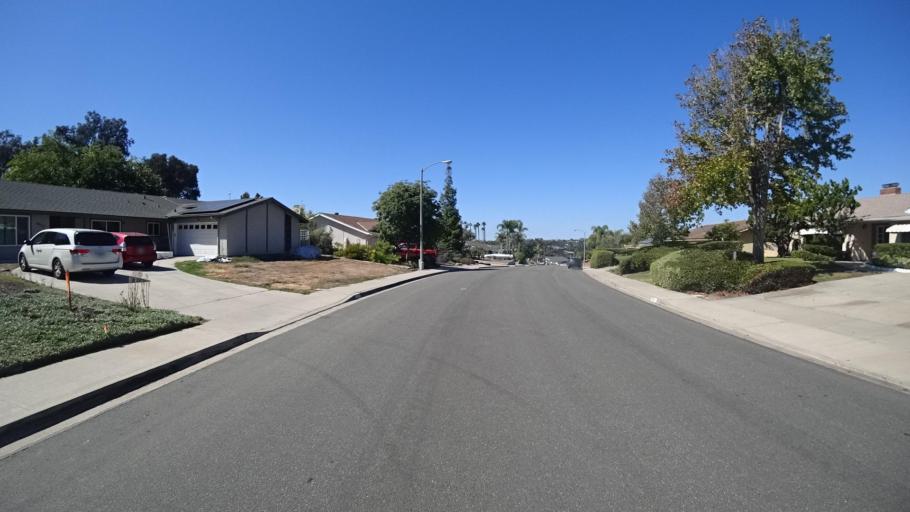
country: US
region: California
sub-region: San Diego County
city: Bonita
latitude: 32.6632
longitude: -117.0178
